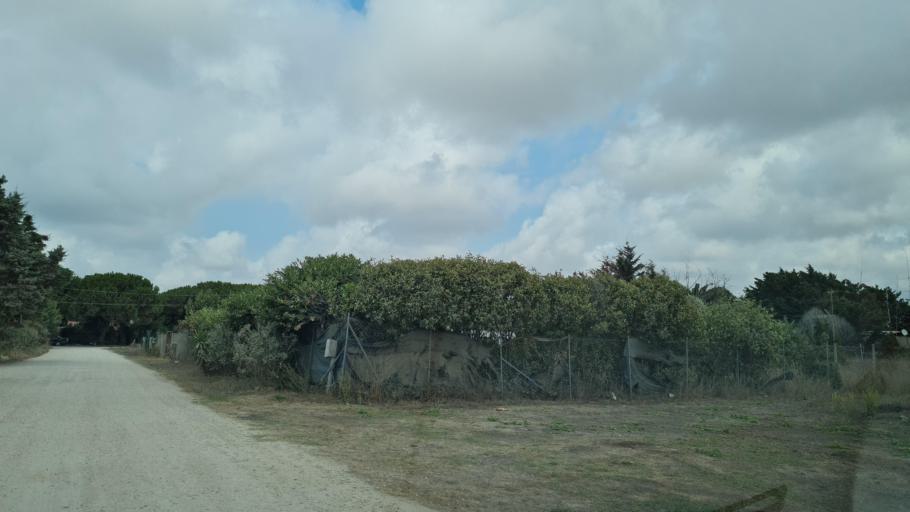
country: IT
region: Latium
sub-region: Provincia di Viterbo
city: Tarquinia
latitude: 42.1935
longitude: 11.7294
